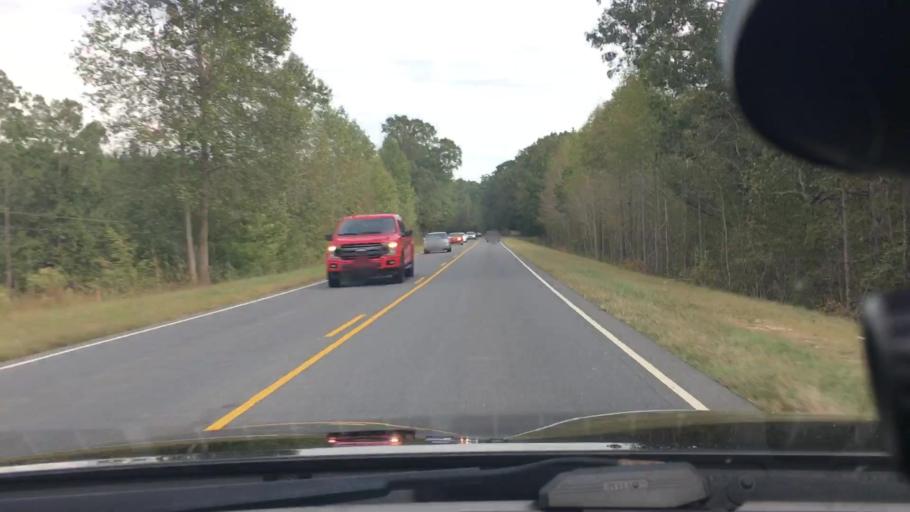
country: US
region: North Carolina
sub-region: Montgomery County
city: Mount Gilead
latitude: 35.3050
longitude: -80.0345
